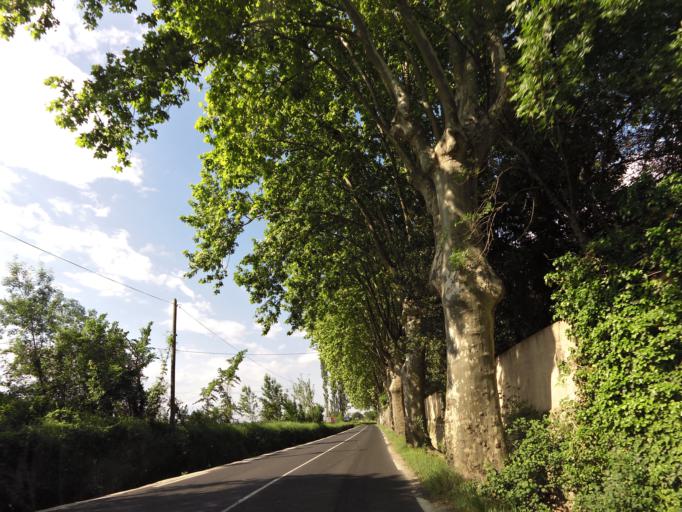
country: FR
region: Languedoc-Roussillon
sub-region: Departement de l'Herault
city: Boisseron
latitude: 43.7699
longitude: 4.0840
